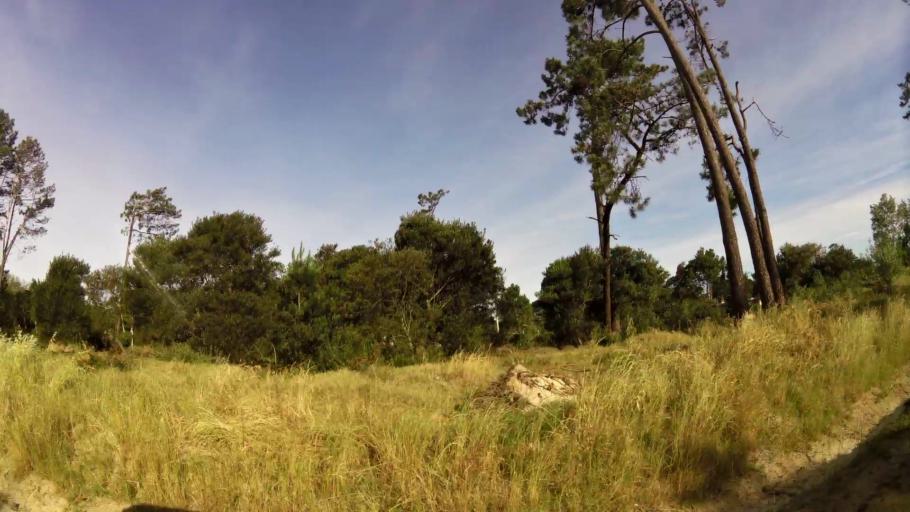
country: UY
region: Canelones
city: Empalme Olmos
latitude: -34.7861
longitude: -55.8566
